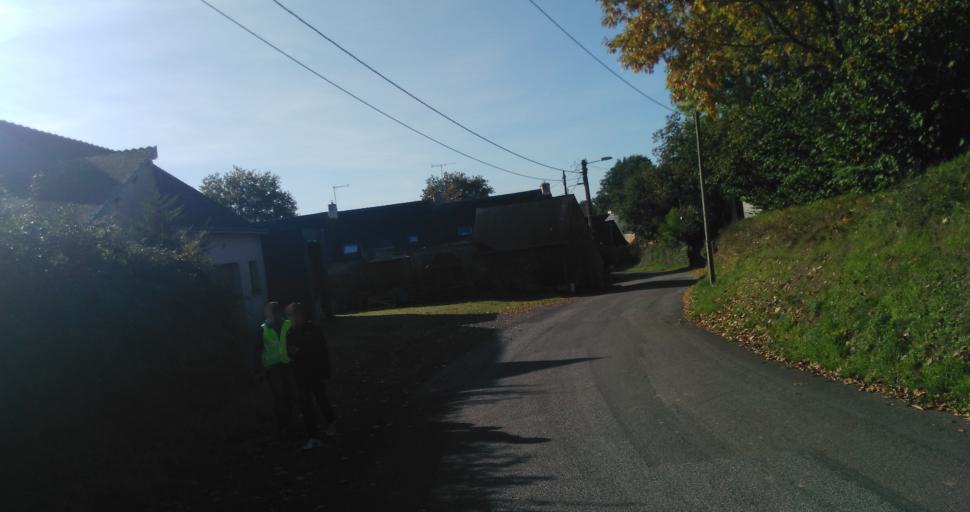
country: FR
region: Brittany
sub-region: Departement du Morbihan
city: Peillac
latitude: 47.7431
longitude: -2.2095
